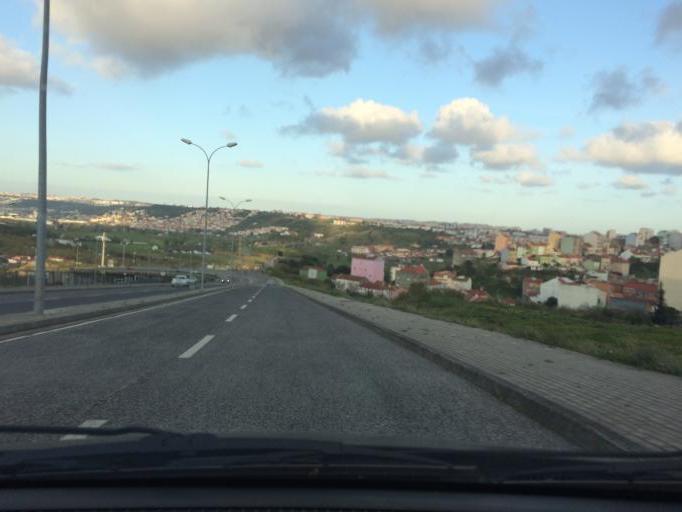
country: PT
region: Lisbon
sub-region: Odivelas
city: Famoes
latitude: 38.7718
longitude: -9.2188
